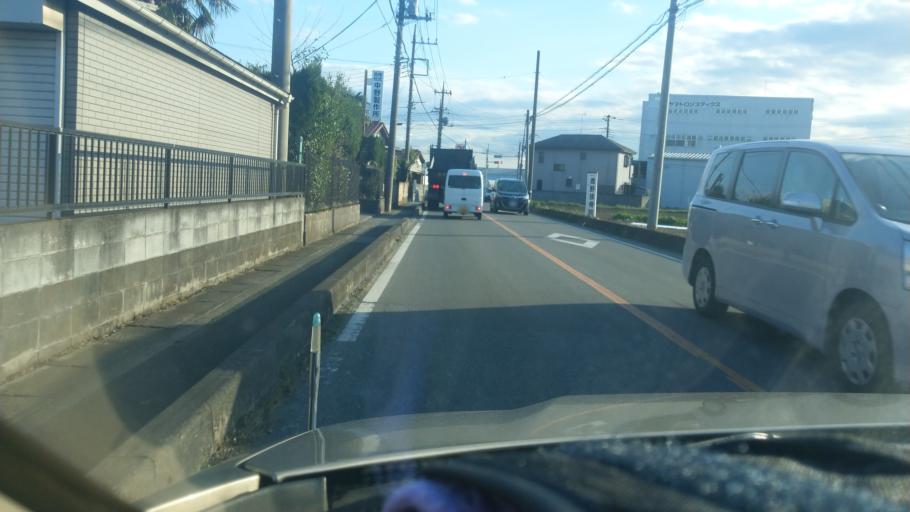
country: JP
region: Saitama
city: Yono
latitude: 35.8956
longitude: 139.5914
